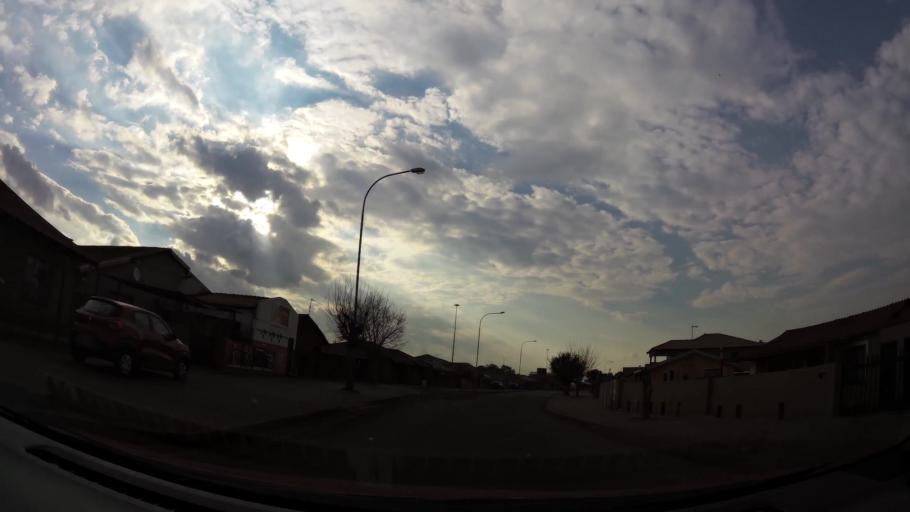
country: ZA
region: Gauteng
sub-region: Sedibeng District Municipality
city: Vanderbijlpark
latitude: -26.6962
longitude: 27.8659
